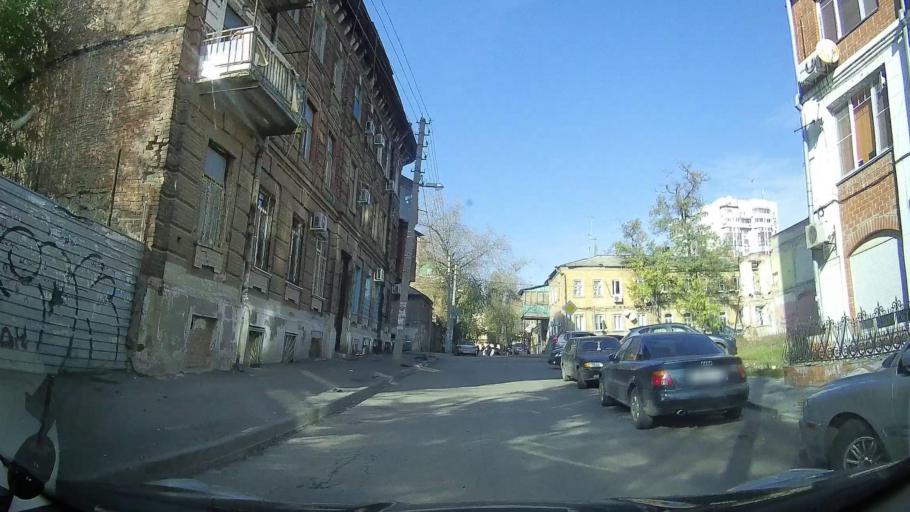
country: RU
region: Rostov
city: Rostov-na-Donu
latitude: 47.2213
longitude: 39.7273
